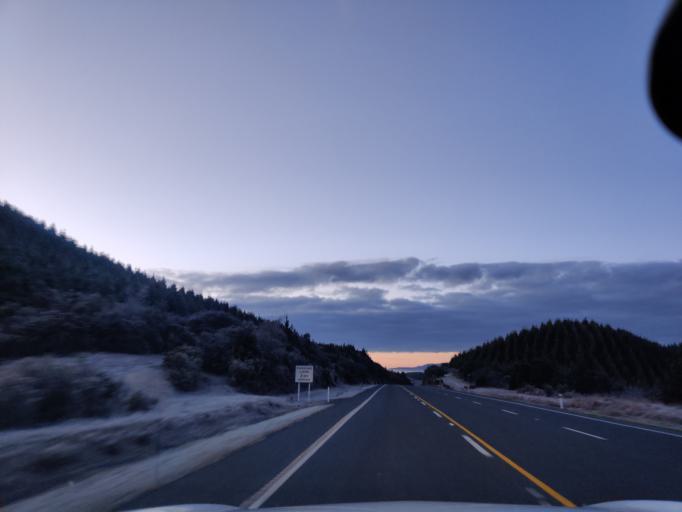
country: NZ
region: Waikato
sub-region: South Waikato District
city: Tokoroa
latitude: -38.3200
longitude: 175.9841
